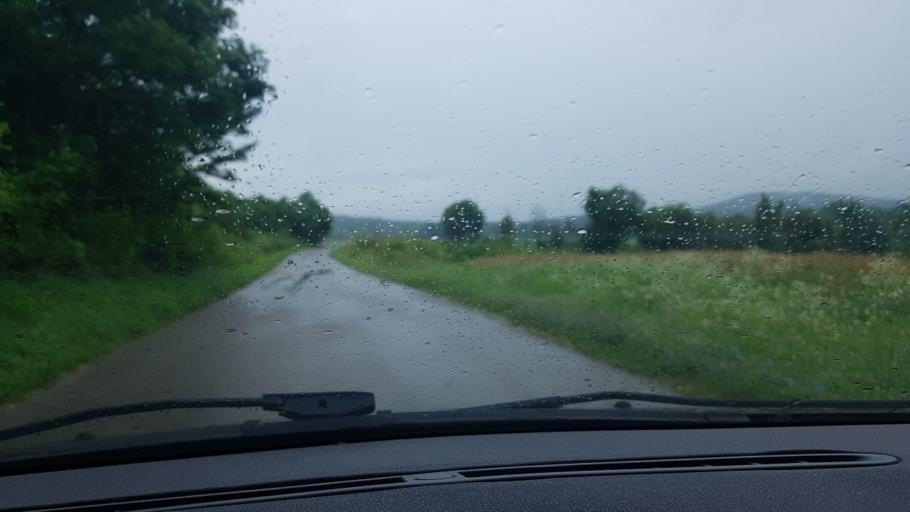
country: HR
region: Licko-Senjska
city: Jezerce
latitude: 44.9896
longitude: 15.6662
